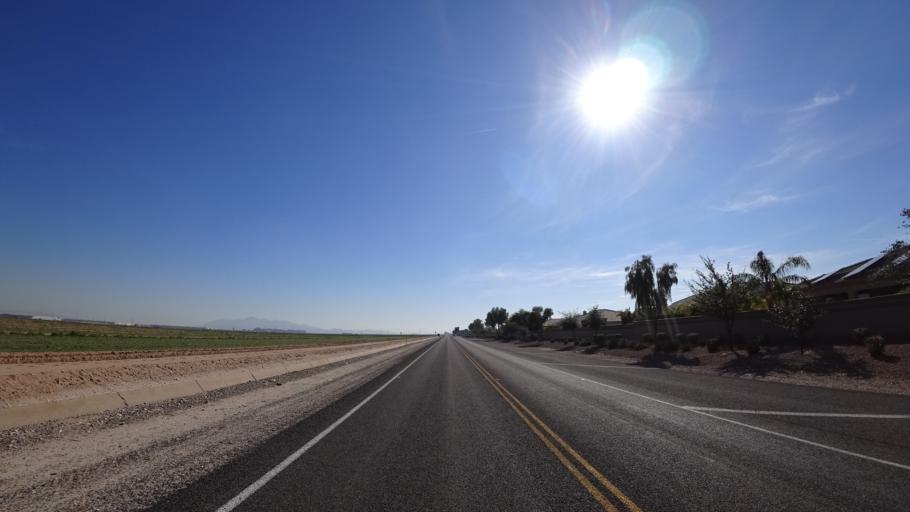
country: US
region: Arizona
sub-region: Maricopa County
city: Citrus Park
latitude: 33.5185
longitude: -112.4442
